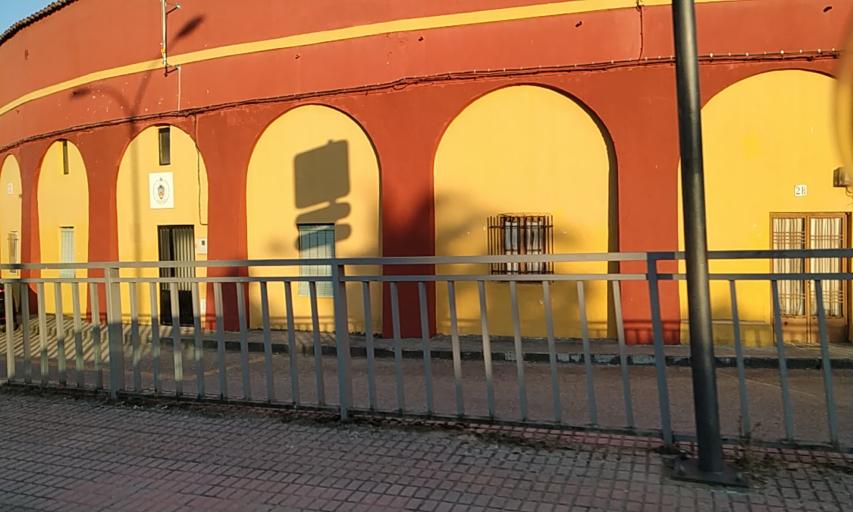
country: ES
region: Extremadura
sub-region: Provincia de Caceres
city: Valencia de Alcantara
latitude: 39.4097
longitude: -7.2463
